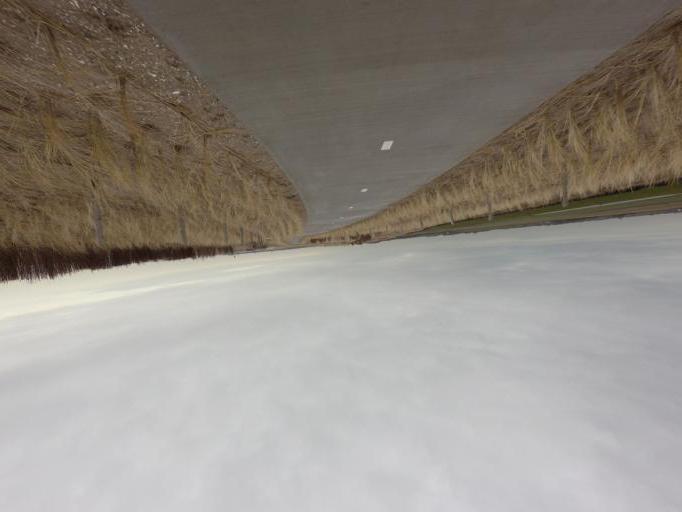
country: NL
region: North Holland
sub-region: Gemeente Texel
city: Den Burg
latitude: 53.0174
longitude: 4.8048
